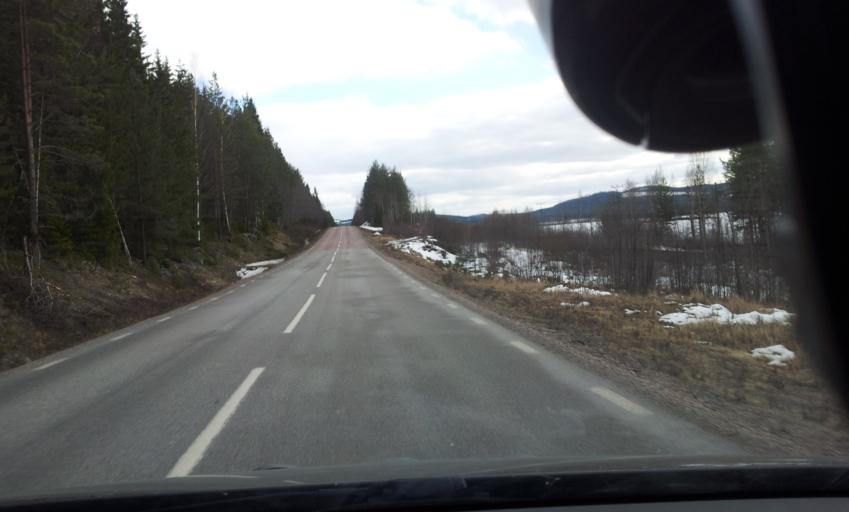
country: SE
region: Vaesternorrland
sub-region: Ange Kommun
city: Ange
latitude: 62.1493
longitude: 15.6832
